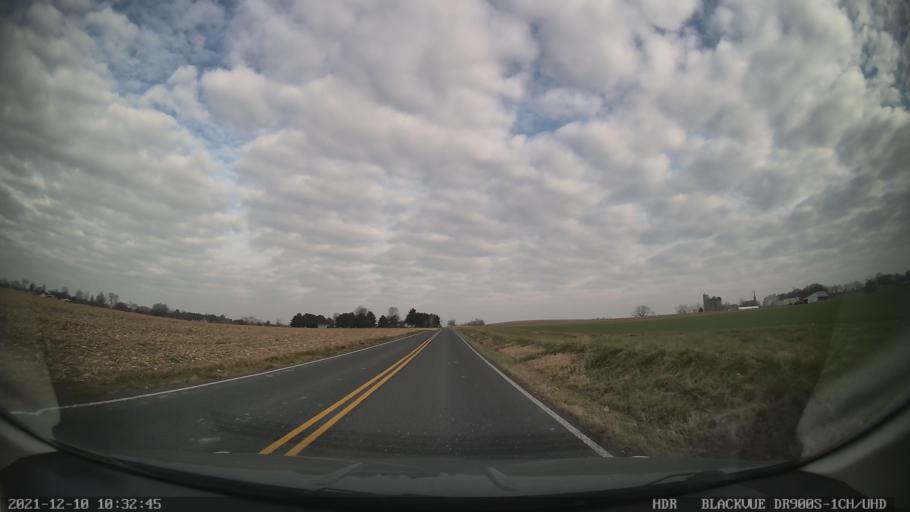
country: US
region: Pennsylvania
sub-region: Berks County
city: Topton
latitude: 40.5342
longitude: -75.7179
